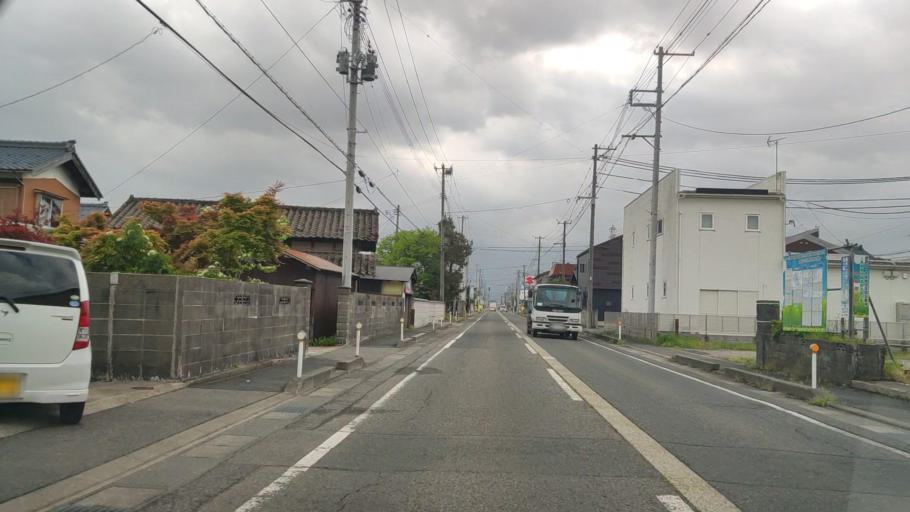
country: JP
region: Niigata
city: Gosen
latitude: 37.7355
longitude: 139.1917
